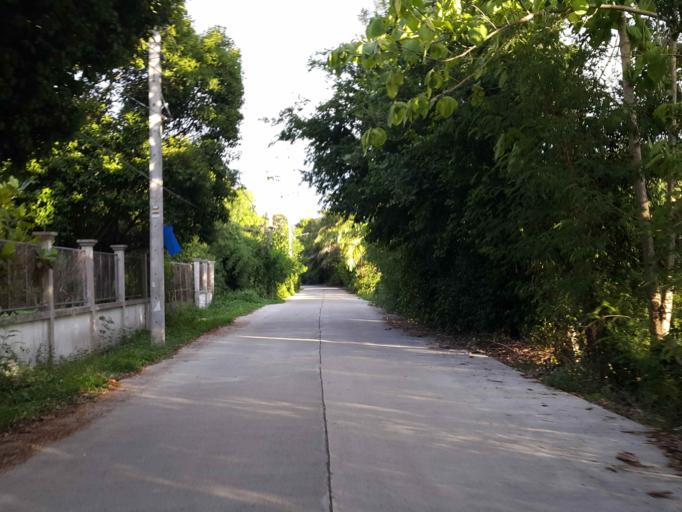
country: TH
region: Chiang Mai
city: Chiang Mai
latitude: 18.8109
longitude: 99.0204
